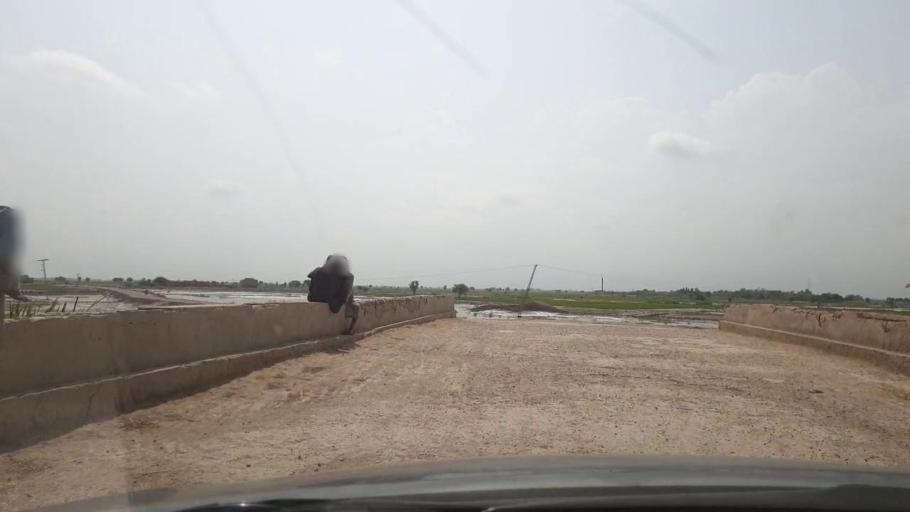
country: PK
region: Sindh
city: Ratodero
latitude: 27.8388
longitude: 68.3356
